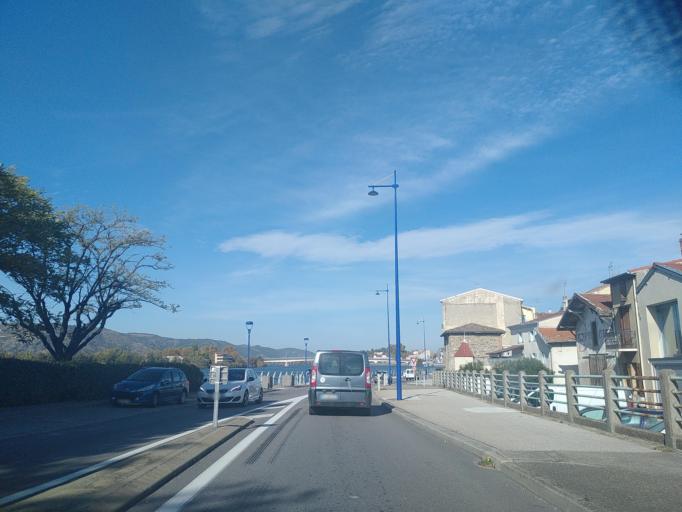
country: FR
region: Rhone-Alpes
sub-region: Departement de la Drome
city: Saint-Vallier
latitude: 45.1776
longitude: 4.8132
